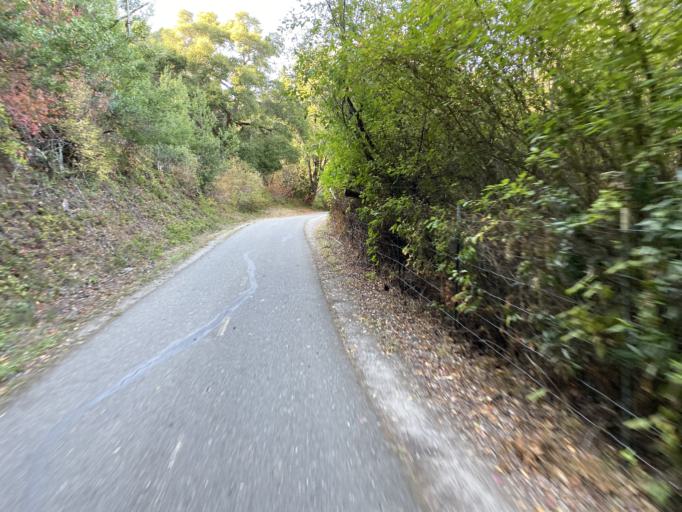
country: US
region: California
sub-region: San Mateo County
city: Hillsborough
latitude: 37.5671
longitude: -122.4016
